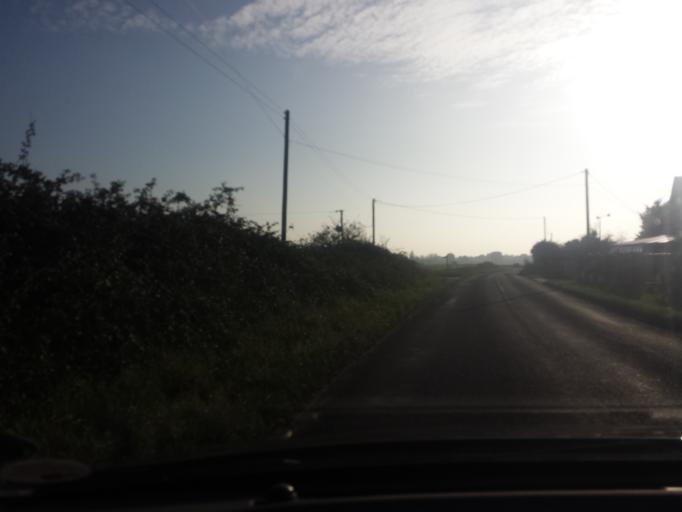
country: GB
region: England
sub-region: Essex
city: Saint Osyth
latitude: 51.7868
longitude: 1.0869
